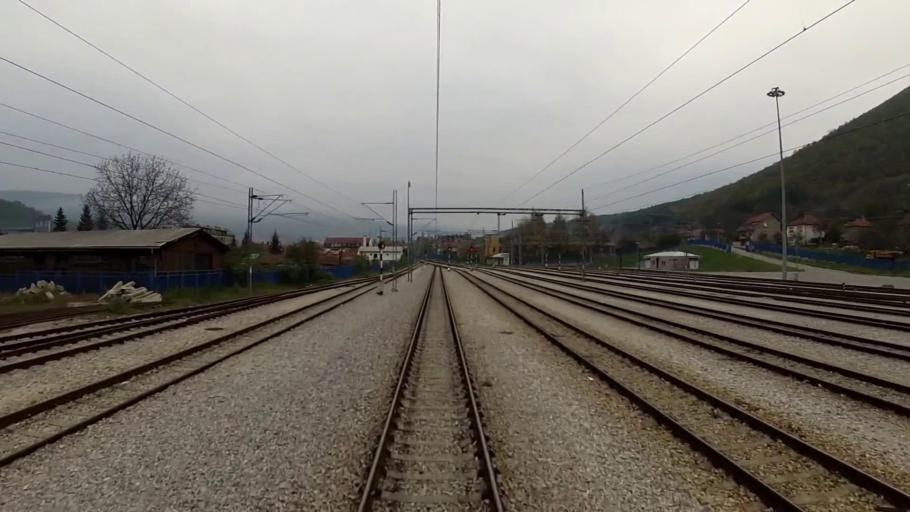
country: RS
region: Central Serbia
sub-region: Pirotski Okrug
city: Dimitrovgrad
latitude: 43.0150
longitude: 22.7740
